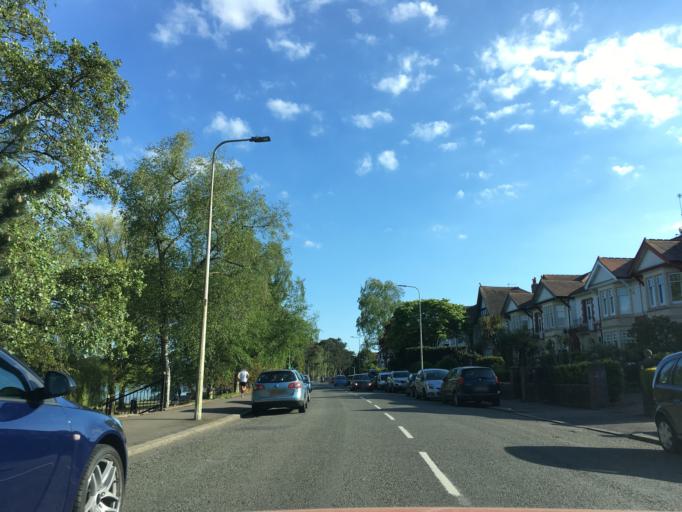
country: GB
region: Wales
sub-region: Cardiff
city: Cardiff
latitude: 51.5120
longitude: -3.1765
